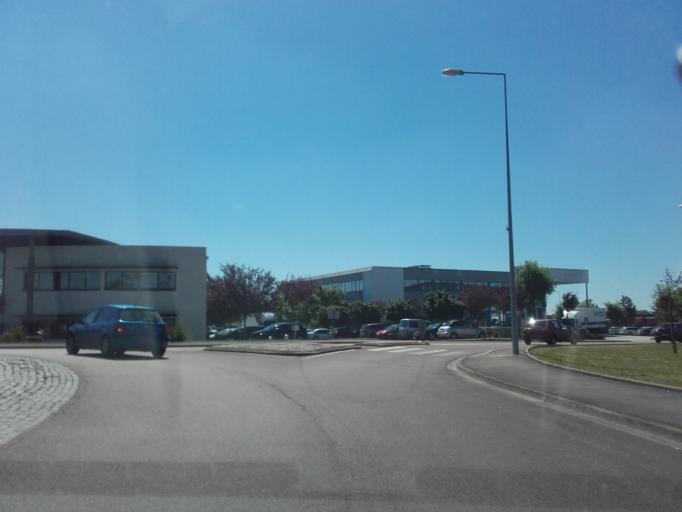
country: FR
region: Bourgogne
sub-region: Departement de la Cote-d'Or
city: Beaune
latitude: 47.0411
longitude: 4.8441
